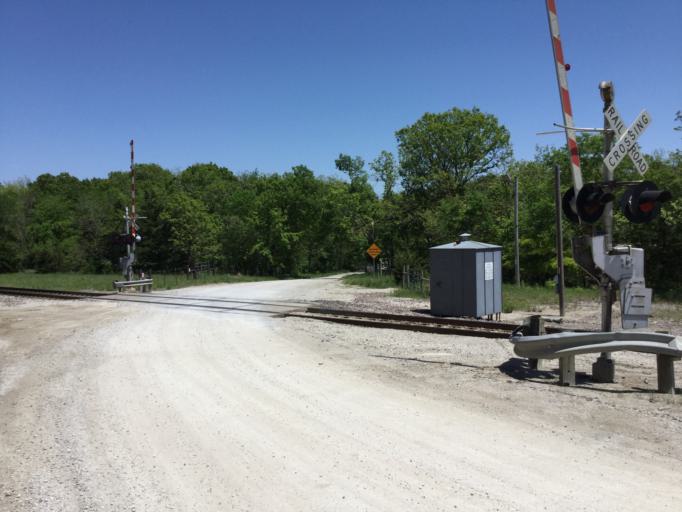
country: US
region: Missouri
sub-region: Cass County
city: Belton
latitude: 38.8109
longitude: -94.6389
